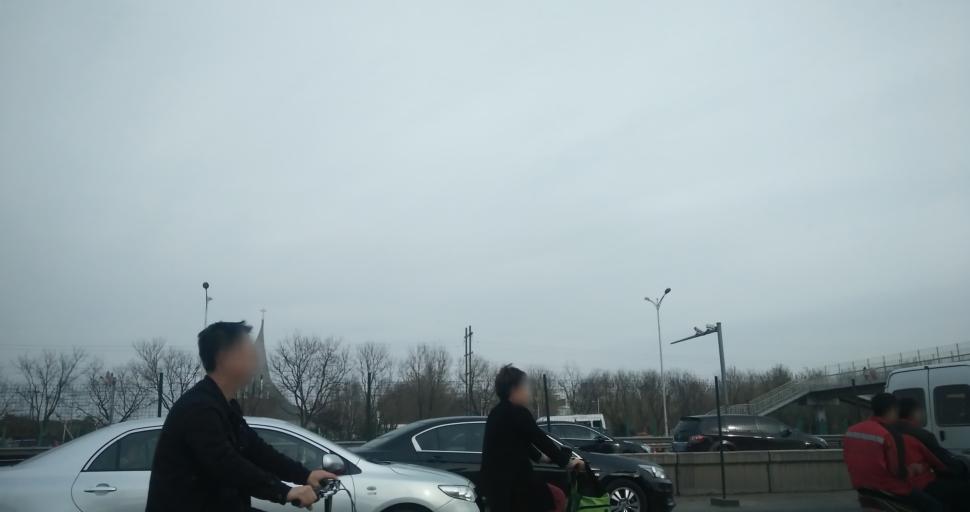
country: CN
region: Beijing
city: Huaxiang
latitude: 39.8359
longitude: 116.3393
